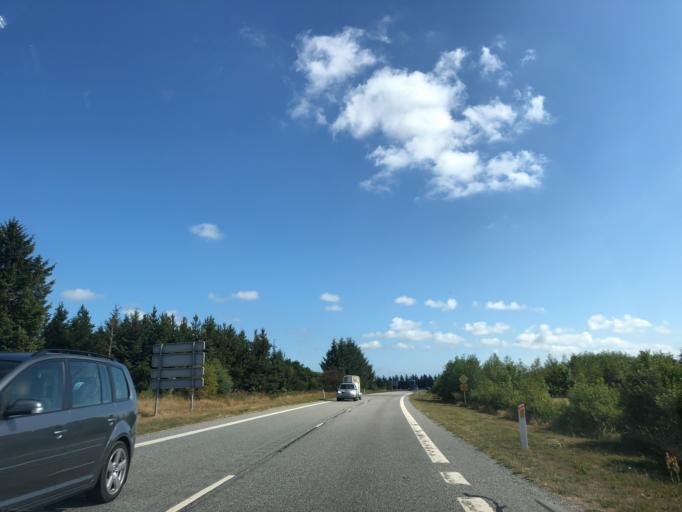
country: DK
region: North Denmark
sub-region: Jammerbugt Kommune
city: Fjerritslev
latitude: 57.0601
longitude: 9.1870
